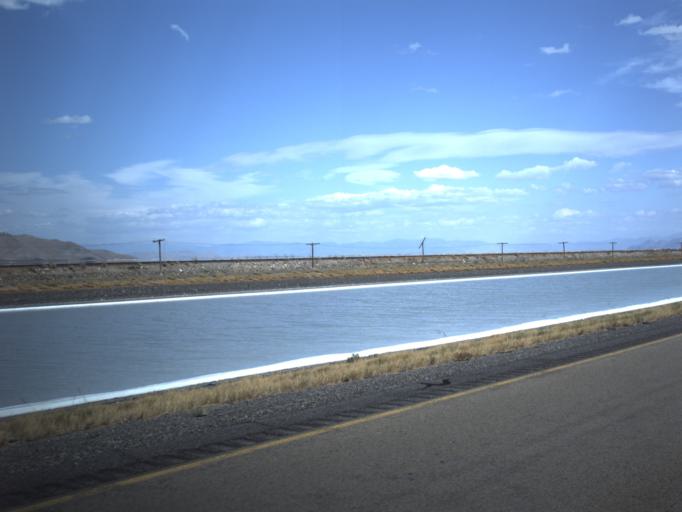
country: US
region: Utah
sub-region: Tooele County
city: Grantsville
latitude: 40.7337
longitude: -112.6022
